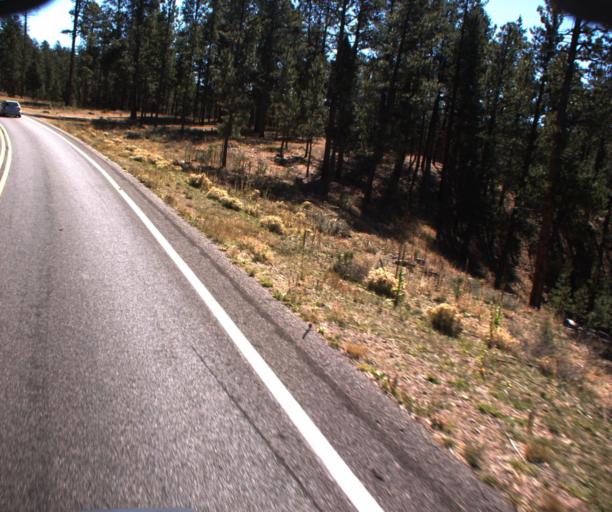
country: US
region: Arizona
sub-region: Coconino County
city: Fredonia
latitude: 36.6712
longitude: -112.2068
